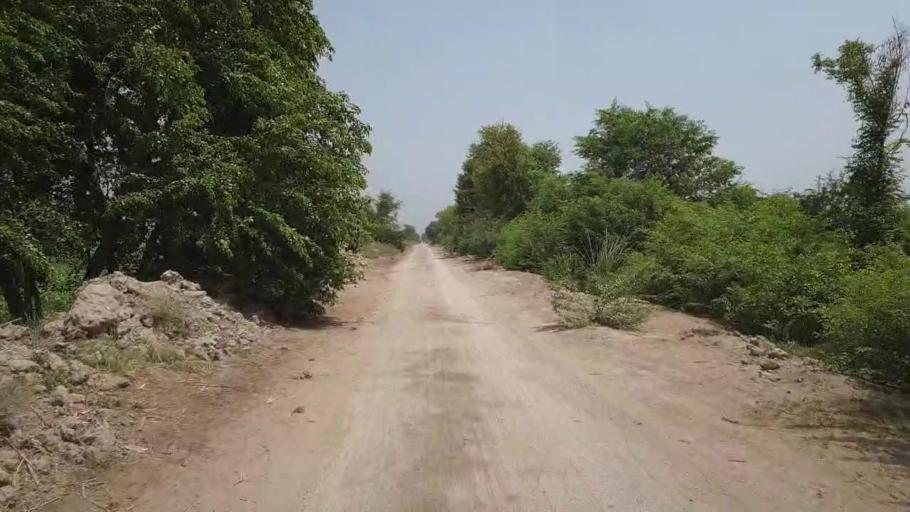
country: PK
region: Sindh
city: Nawabshah
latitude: 26.3071
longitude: 68.3027
